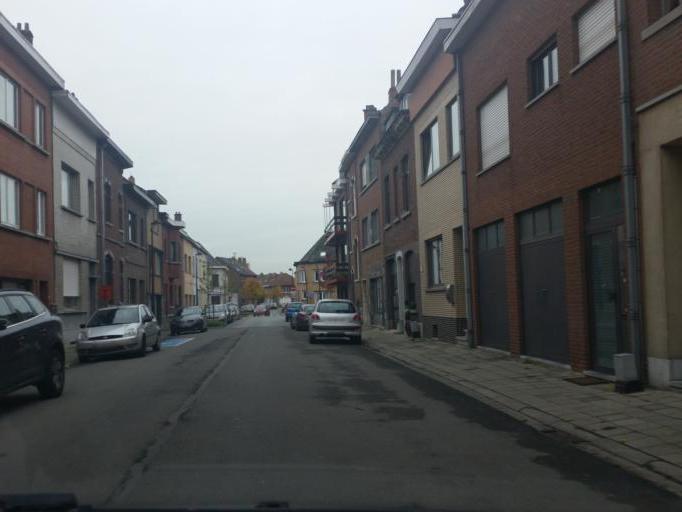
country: BE
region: Flanders
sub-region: Provincie Vlaams-Brabant
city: Beersel
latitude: 50.7626
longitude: 4.2775
